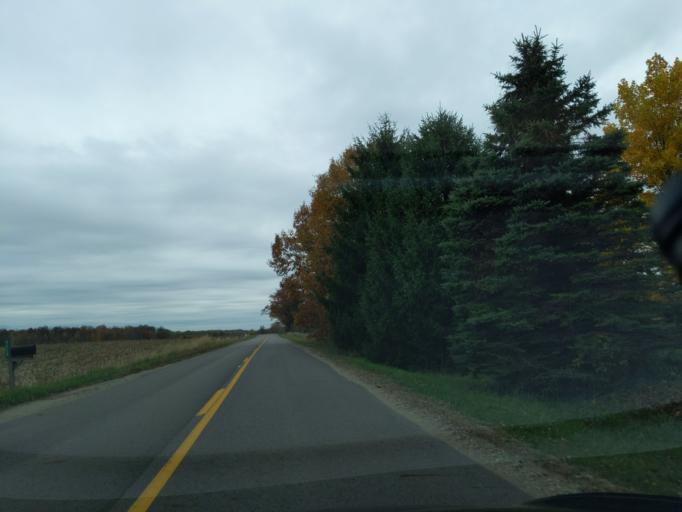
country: US
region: Michigan
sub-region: Eaton County
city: Eaton Rapids
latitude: 42.4291
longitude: -84.6103
